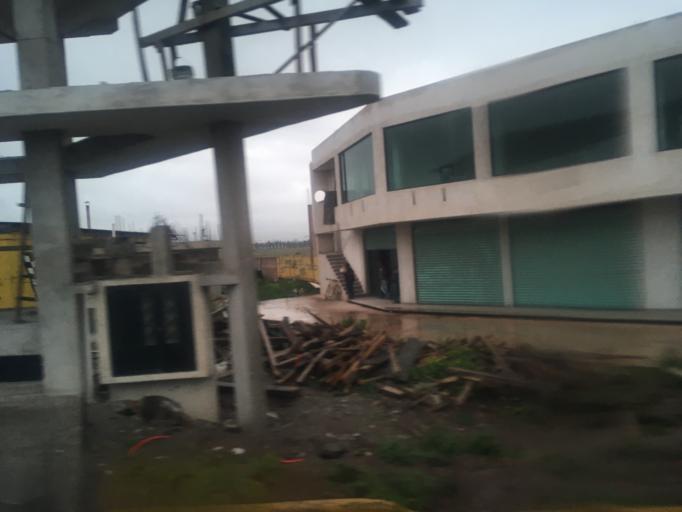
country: MX
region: Puebla
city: Chignahuapan
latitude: 19.8486
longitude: -98.0265
